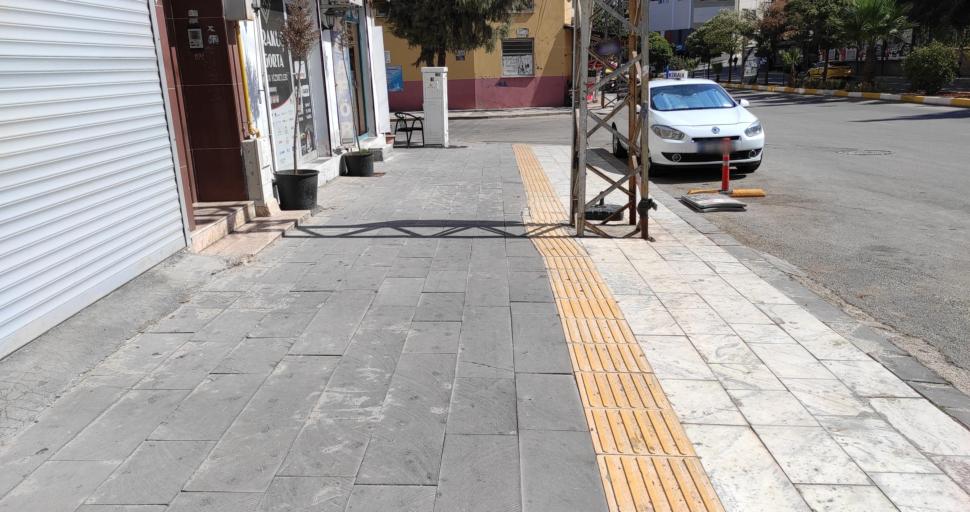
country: TR
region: Kilis
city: Kilis
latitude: 36.7231
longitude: 37.1055
